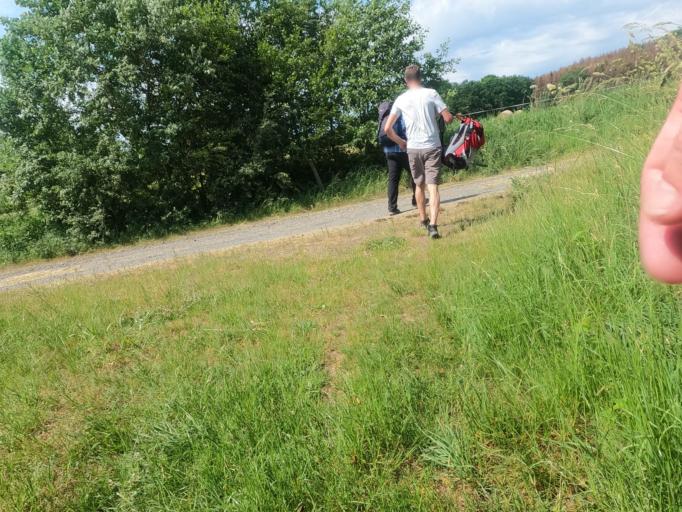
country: DE
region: Rheinland-Pfalz
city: Lochum
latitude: 50.6161
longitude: 7.8741
